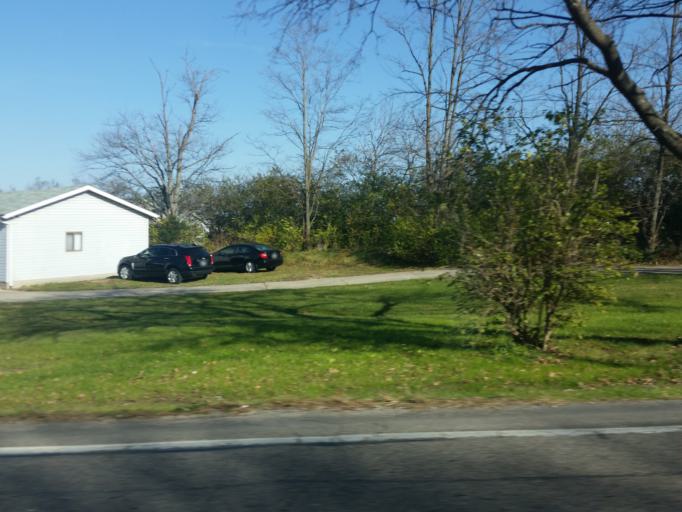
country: US
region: Ohio
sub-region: Butler County
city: Oxford
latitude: 39.4818
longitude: -84.7145
